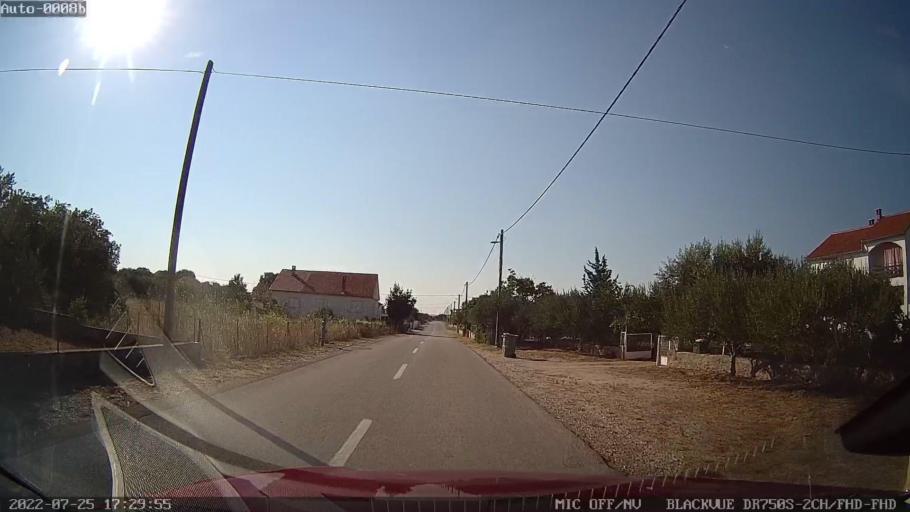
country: HR
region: Zadarska
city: Pridraga
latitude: 44.1617
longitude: 15.5133
